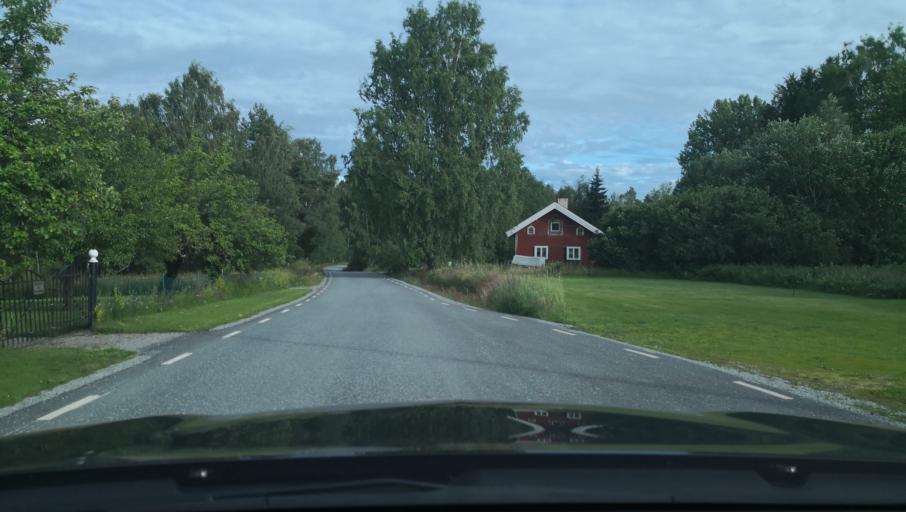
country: SE
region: Vaestmanland
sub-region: Surahammars Kommun
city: Surahammar
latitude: 59.6615
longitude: 16.1749
